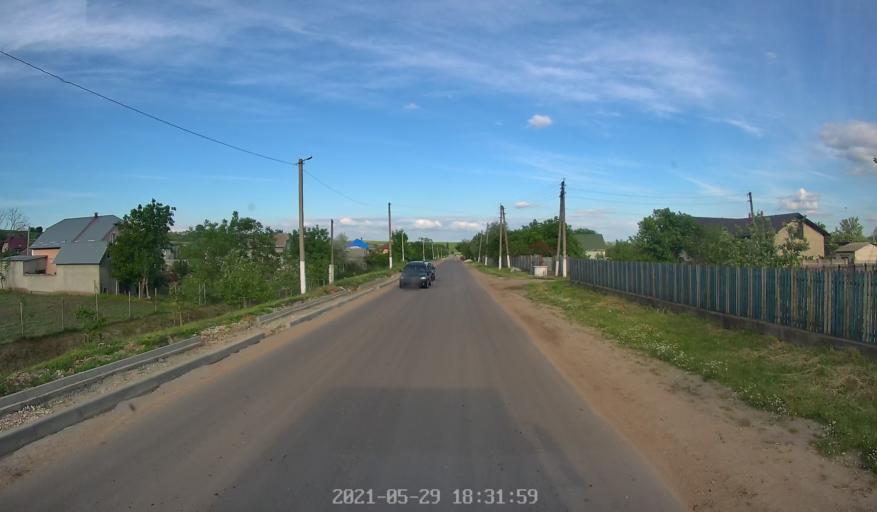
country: MD
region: Chisinau
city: Singera
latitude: 46.8184
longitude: 28.8895
